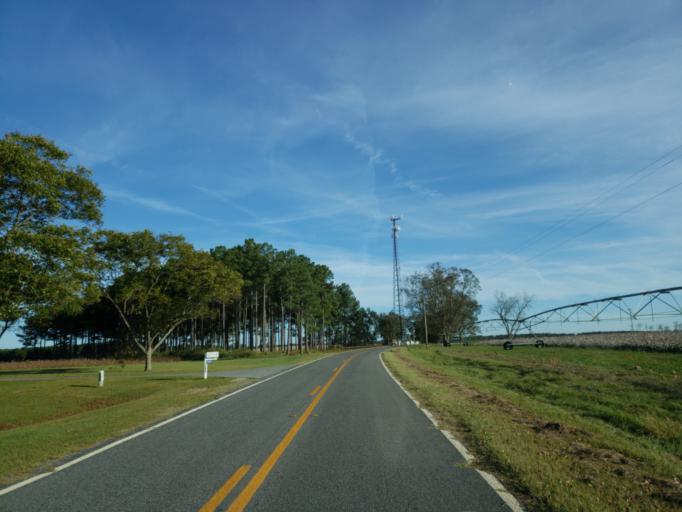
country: US
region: Georgia
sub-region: Dooly County
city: Vienna
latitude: 32.0739
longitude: -83.7818
